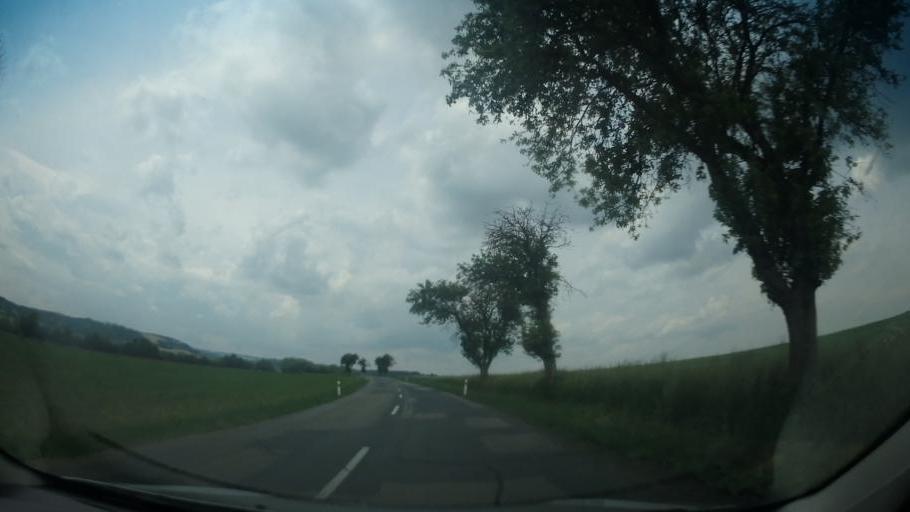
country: CZ
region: South Moravian
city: Cerna Hora
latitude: 49.4377
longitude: 16.5641
